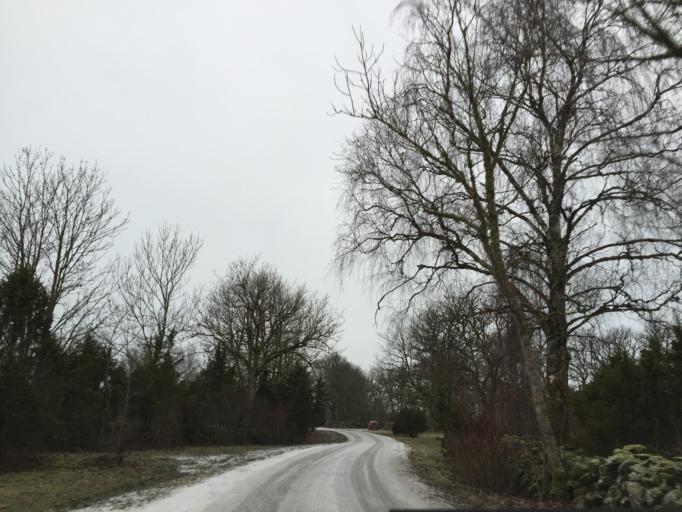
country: EE
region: Saare
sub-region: Orissaare vald
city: Orissaare
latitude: 58.5955
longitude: 23.0825
